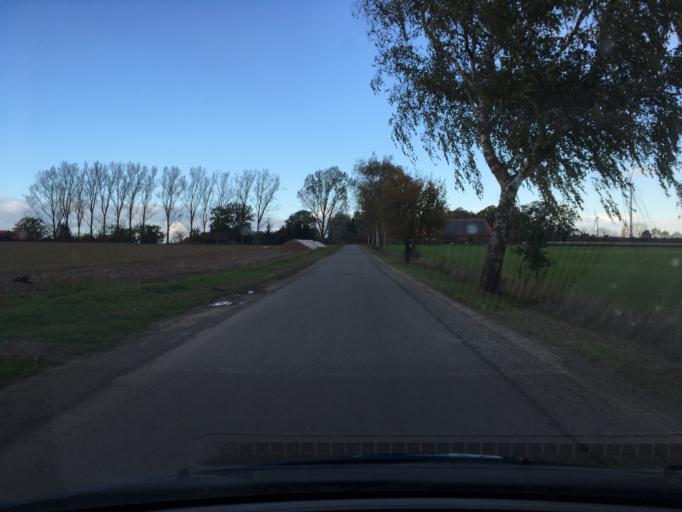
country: DE
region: Lower Saxony
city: Reinstorf
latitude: 53.2470
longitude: 10.5675
